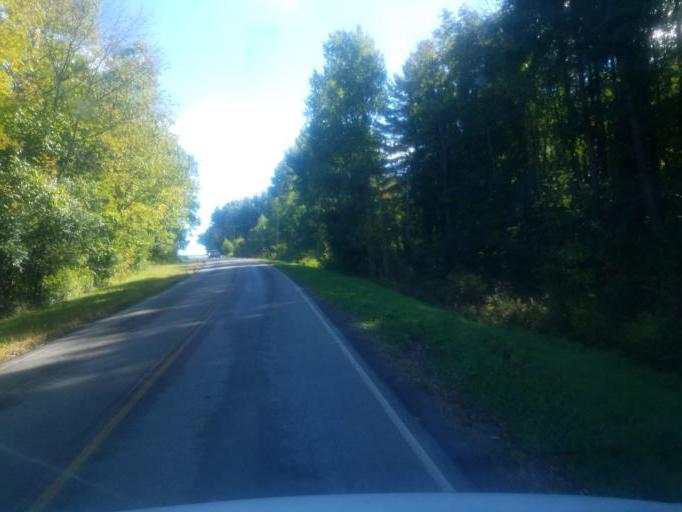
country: US
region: New York
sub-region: Allegany County
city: Friendship
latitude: 42.2772
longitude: -78.1795
